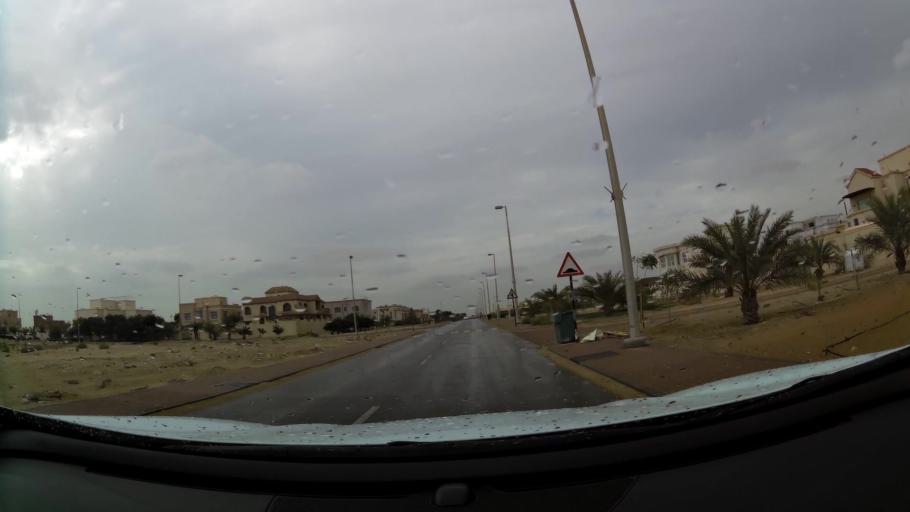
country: AE
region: Abu Dhabi
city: Abu Dhabi
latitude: 24.3586
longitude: 54.6249
